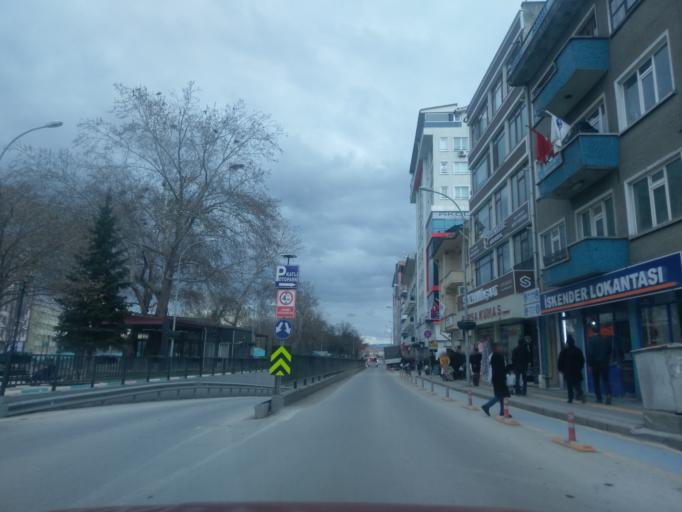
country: TR
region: Kuetahya
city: Kutahya
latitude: 39.4192
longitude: 29.9860
